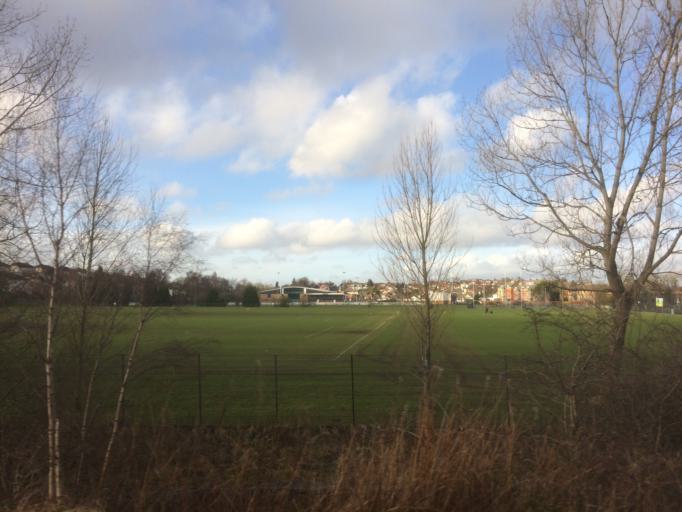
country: GB
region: Scotland
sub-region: East Renfrewshire
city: Giffnock
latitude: 55.8072
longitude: -4.2757
